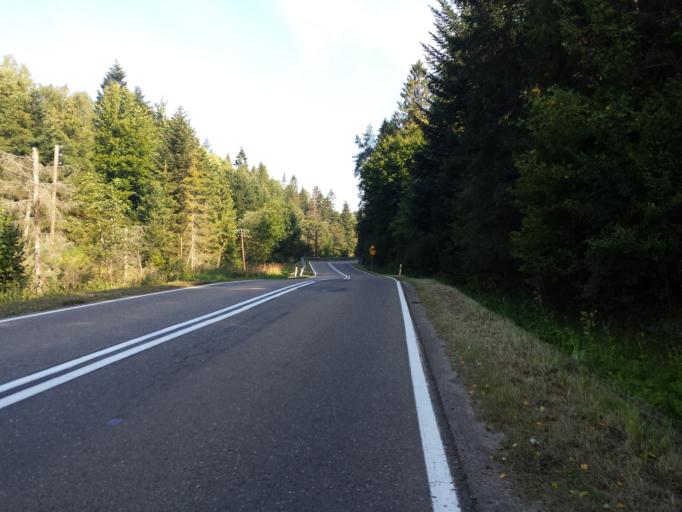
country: PL
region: Subcarpathian Voivodeship
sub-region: Powiat leski
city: Cisna
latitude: 49.2281
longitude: 22.3036
